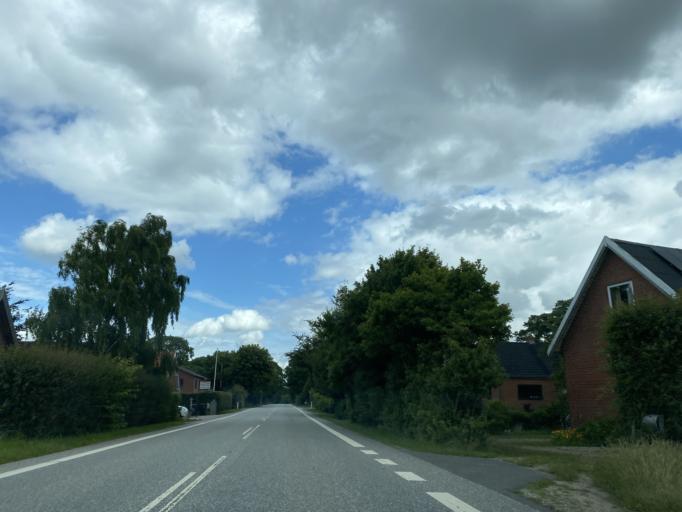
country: DK
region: Central Jutland
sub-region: Silkeborg Kommune
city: Silkeborg
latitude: 56.2517
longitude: 9.6266
